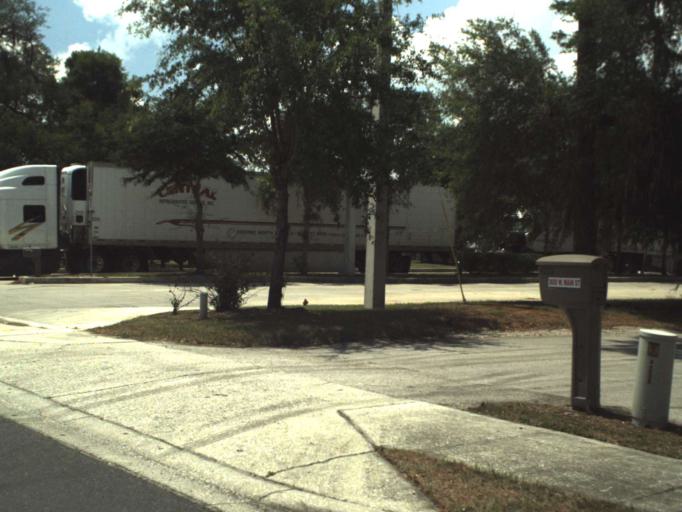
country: US
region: Florida
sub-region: Lake County
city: Leesburg
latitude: 28.8115
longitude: -81.9214
